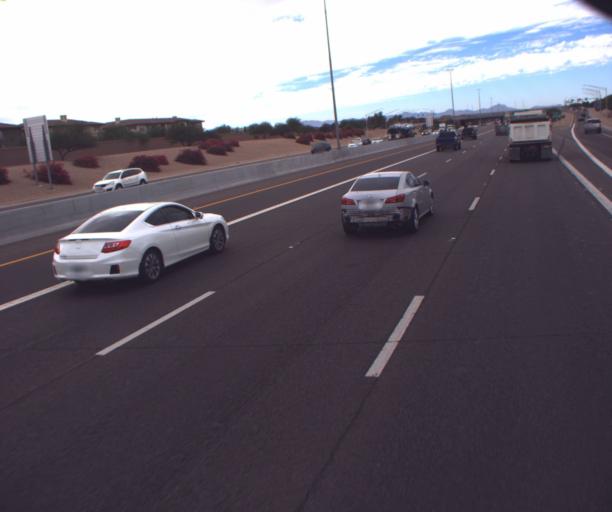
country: US
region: Arizona
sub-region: Maricopa County
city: Chandler
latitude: 33.2874
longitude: -111.8533
